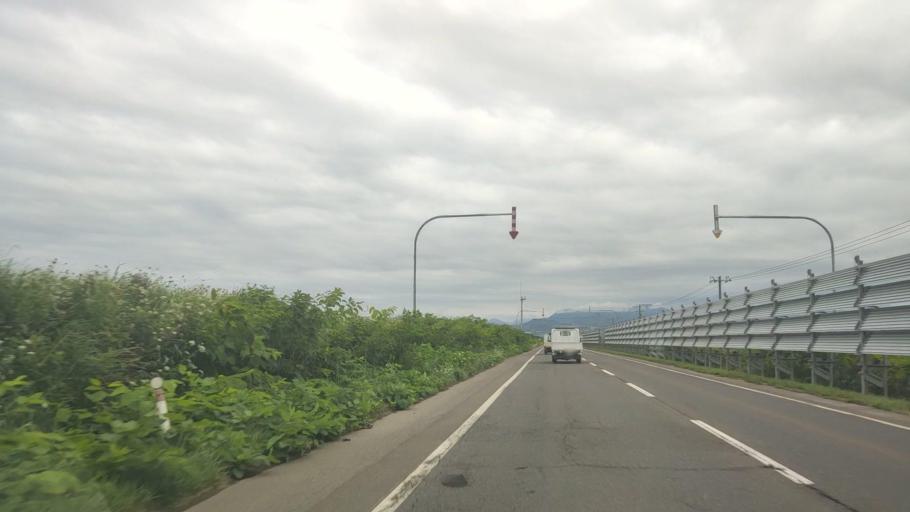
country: JP
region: Hokkaido
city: Nanae
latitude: 42.3019
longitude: 140.2721
